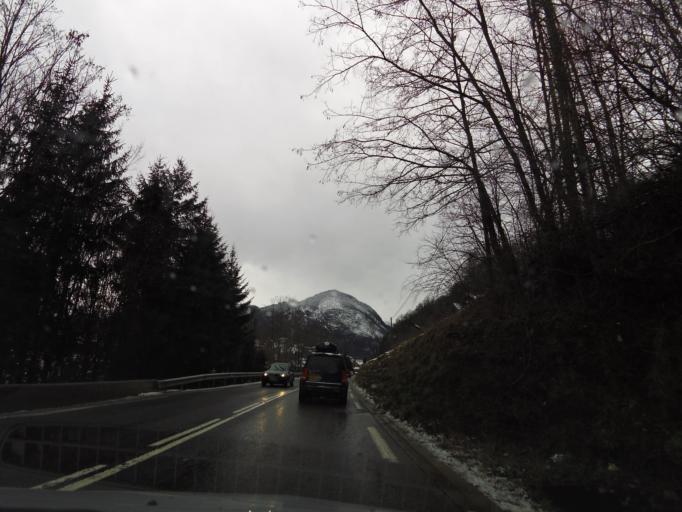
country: FR
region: Rhone-Alpes
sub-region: Departement de la Haute-Savoie
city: Taninges
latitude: 46.1088
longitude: 6.5990
